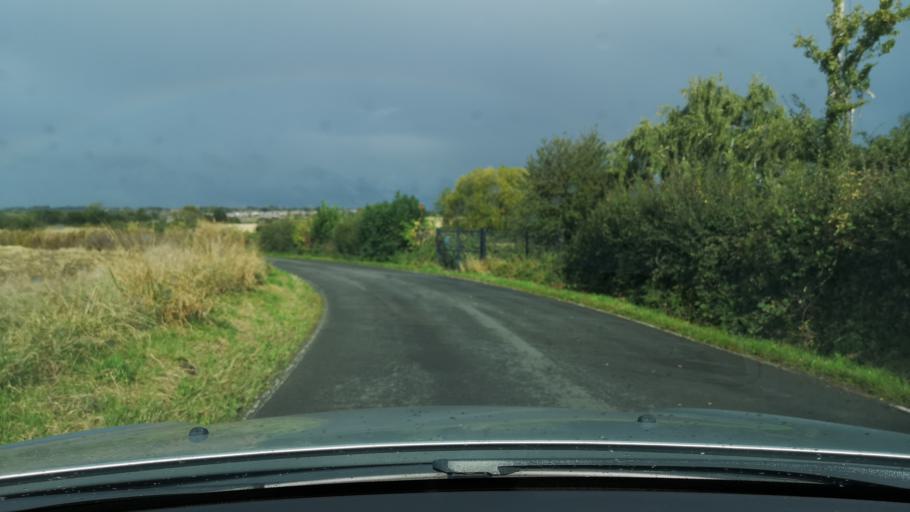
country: GB
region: England
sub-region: City and Borough of Wakefield
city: Darrington
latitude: 53.6640
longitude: -1.2956
